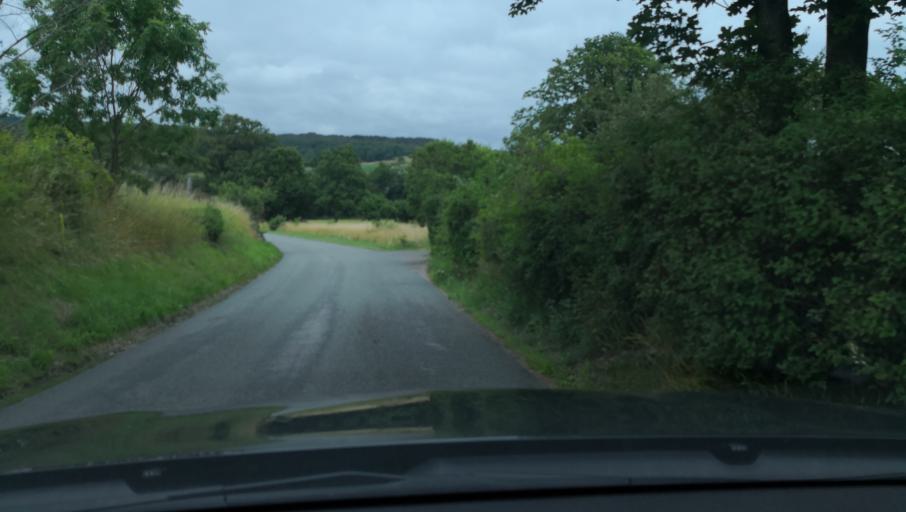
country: SE
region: Skane
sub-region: Simrishamns Kommun
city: Kivik
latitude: 55.7183
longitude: 14.1571
